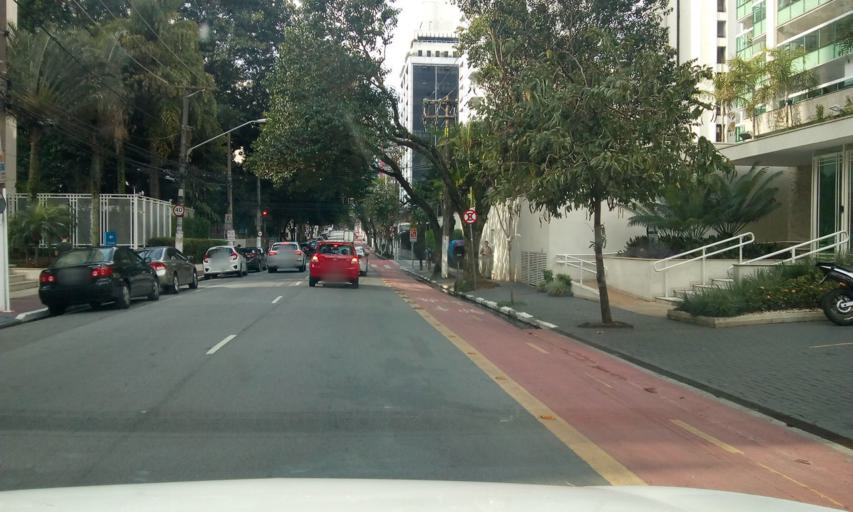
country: BR
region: Sao Paulo
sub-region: Sao Paulo
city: Sao Paulo
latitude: -23.6060
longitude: -46.6614
